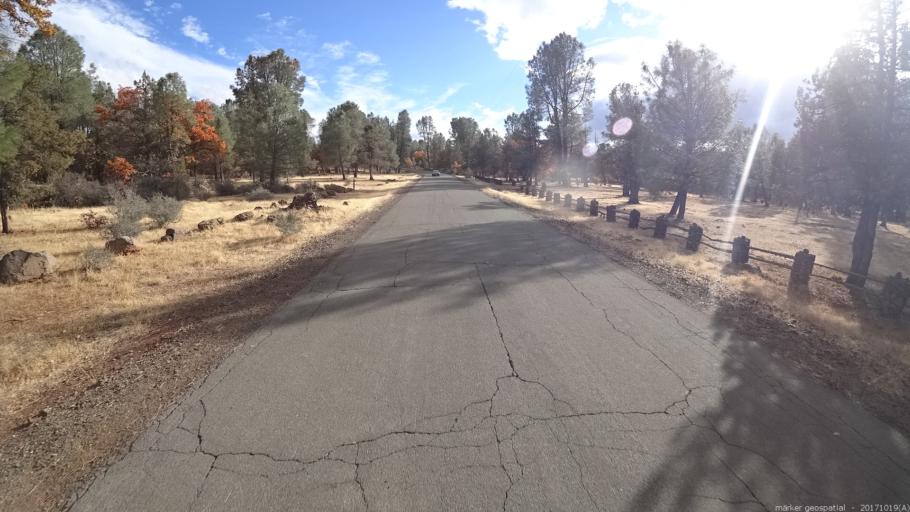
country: US
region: California
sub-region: Shasta County
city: Burney
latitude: 40.9643
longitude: -121.4408
